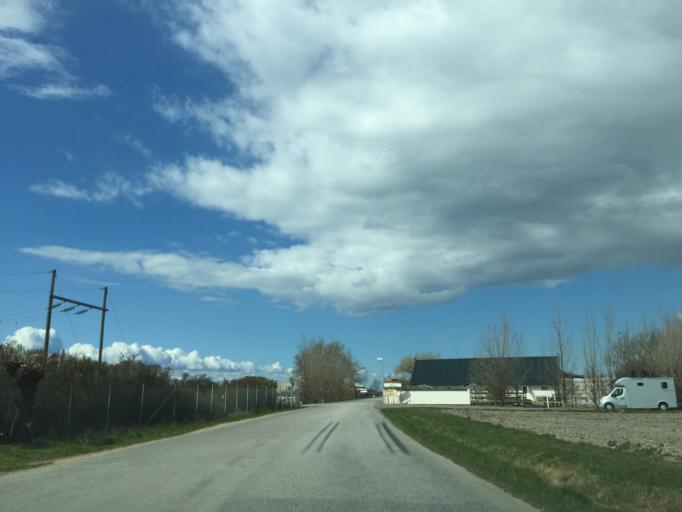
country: SE
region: Skane
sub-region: Vellinge Kommun
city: Hollviken
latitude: 55.4275
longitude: 12.9579
